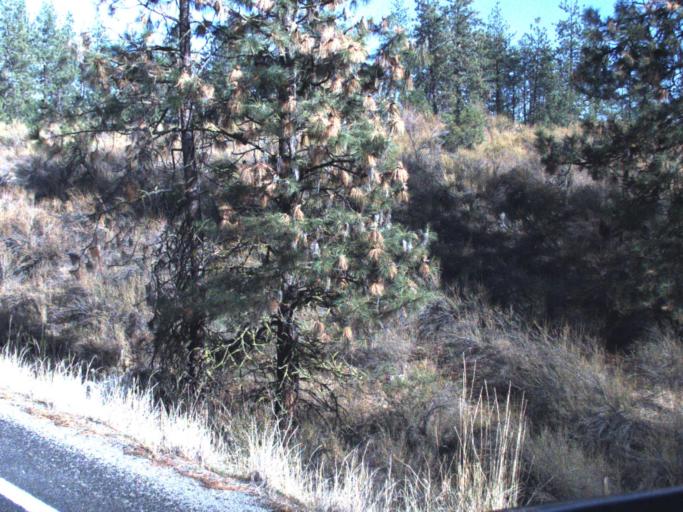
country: US
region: Washington
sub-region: Lincoln County
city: Davenport
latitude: 47.9125
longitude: -118.3339
